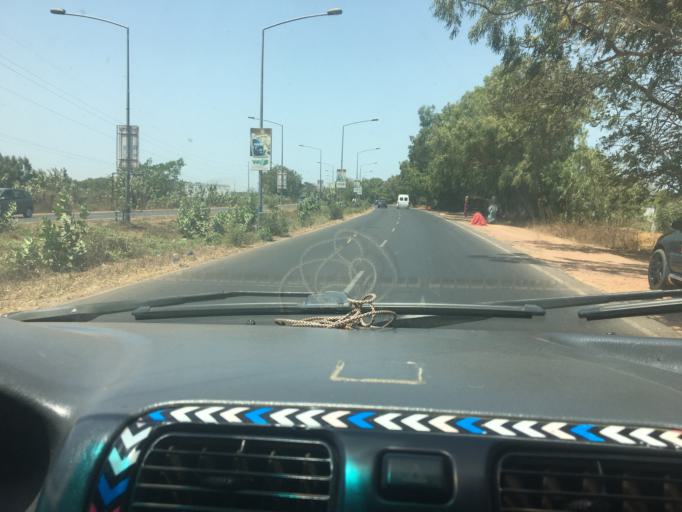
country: GM
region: Banjul
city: Bakau
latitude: 13.4695
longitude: -16.6381
